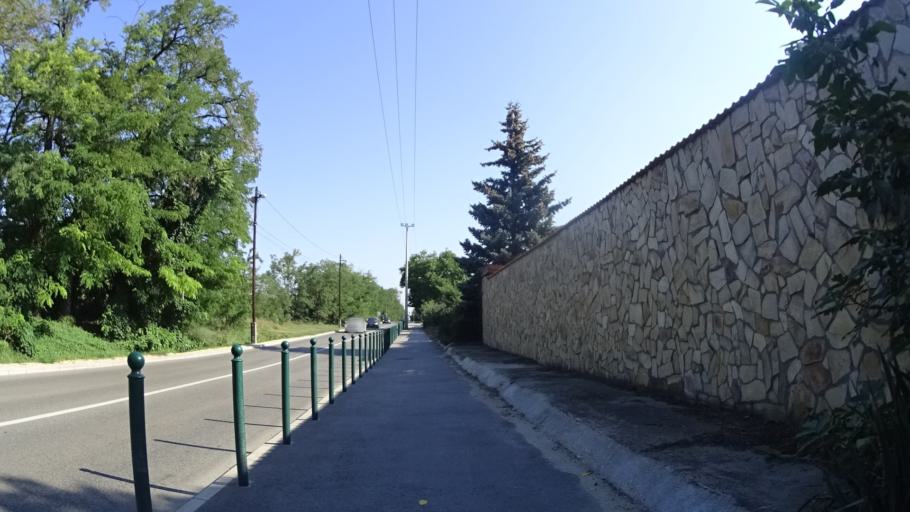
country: HU
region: Pest
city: Dunakeszi
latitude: 47.6099
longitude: 19.1302
